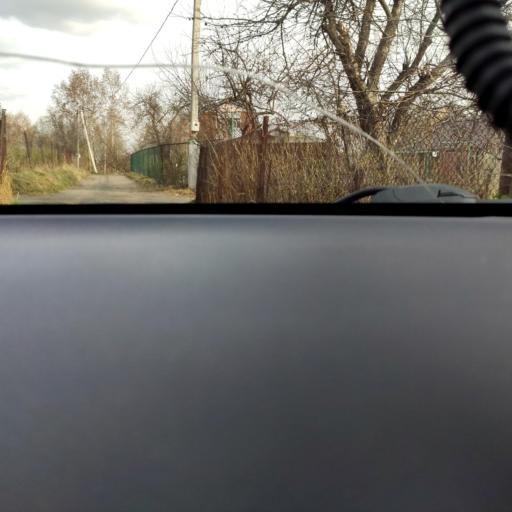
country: RU
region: Tatarstan
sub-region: Gorod Kazan'
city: Kazan
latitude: 55.8888
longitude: 49.0641
